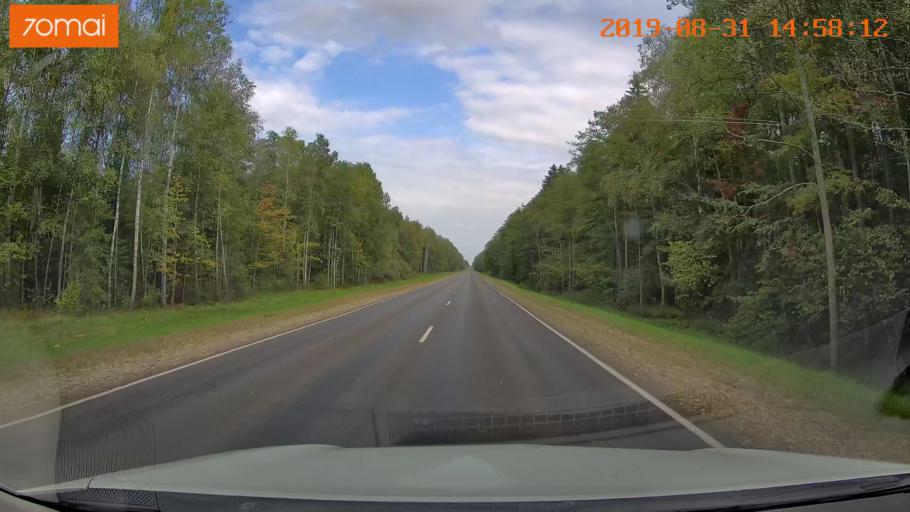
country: RU
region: Kaluga
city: Spas-Demensk
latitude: 54.3159
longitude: 33.9760
